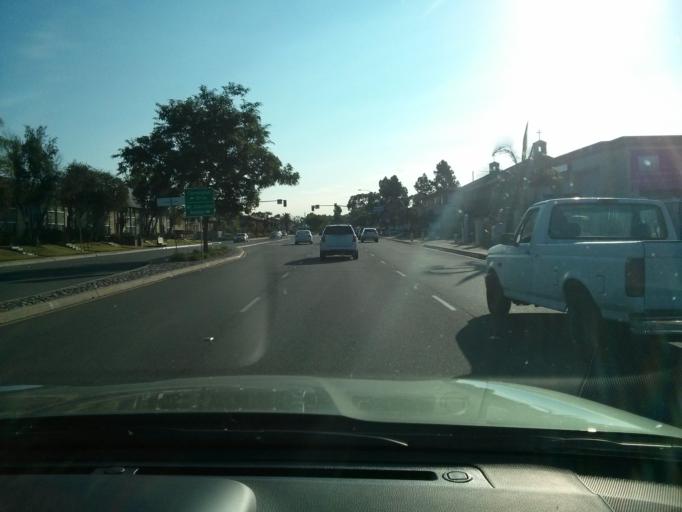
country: US
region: California
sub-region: San Diego County
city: La Jolla
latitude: 32.8203
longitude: -117.1729
